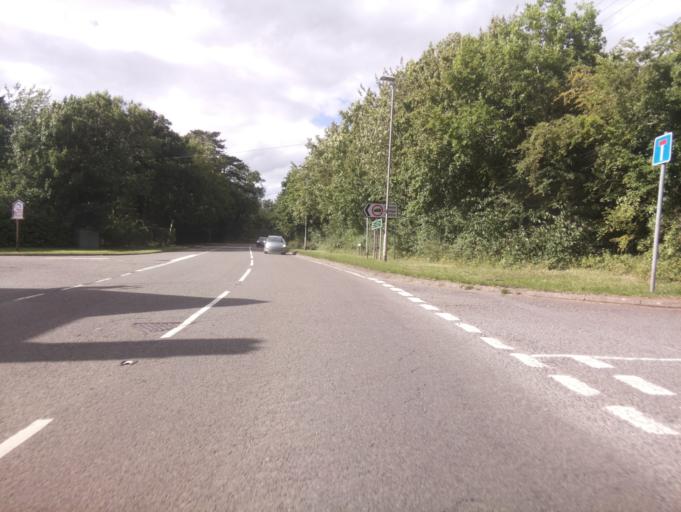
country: GB
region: England
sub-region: Leicestershire
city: Stoke Golding
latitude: 52.6041
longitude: -1.4766
